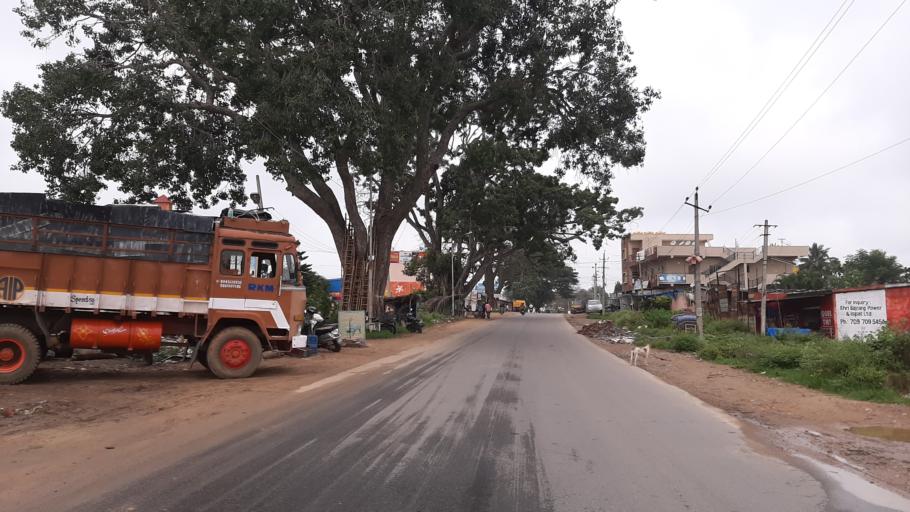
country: IN
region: Karnataka
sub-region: Bangalore Rural
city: Nelamangala
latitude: 12.9650
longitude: 77.3961
